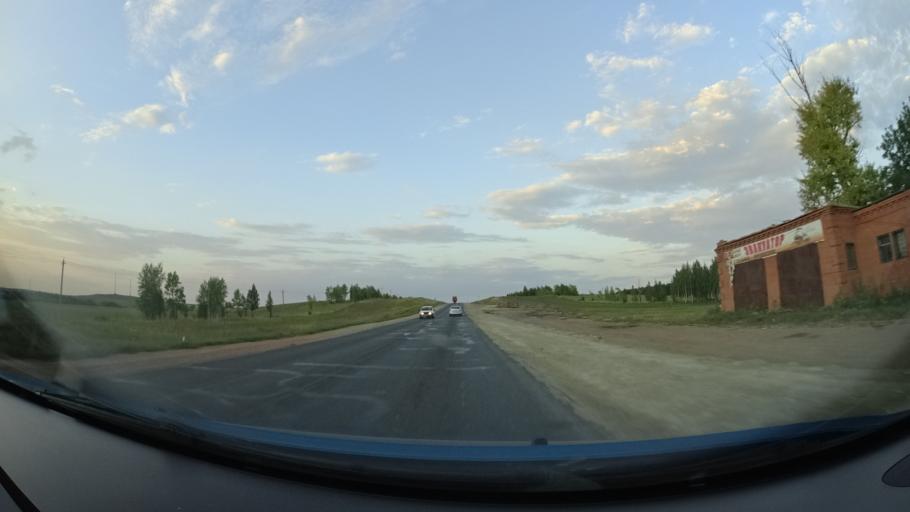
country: RU
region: Orenburg
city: Severnoye
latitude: 54.2143
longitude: 52.7152
